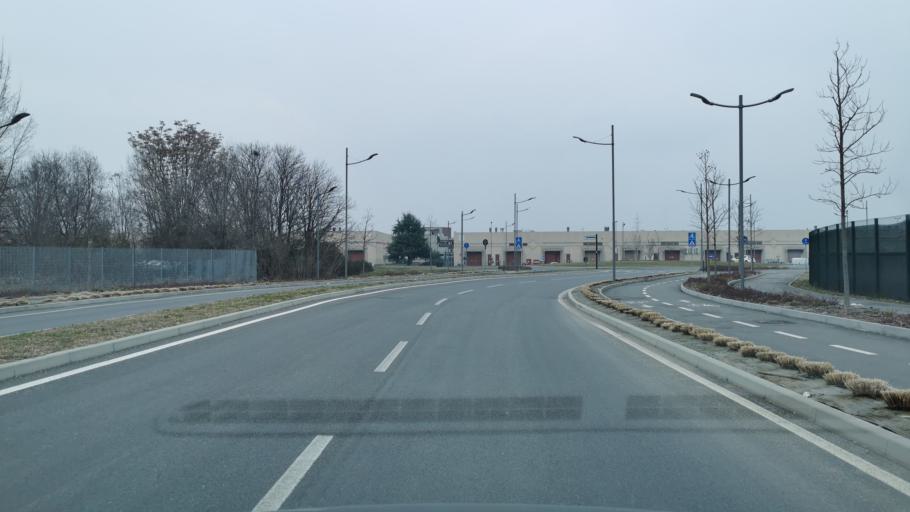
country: IT
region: Piedmont
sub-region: Provincia di Torino
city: Settimo Torinese
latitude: 45.1286
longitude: 7.7467
